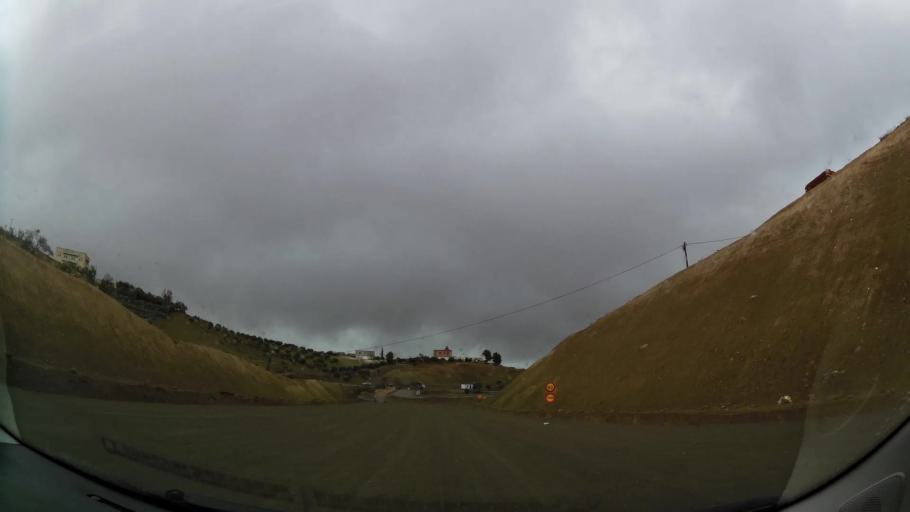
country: MA
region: Oriental
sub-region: Nador
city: Midar
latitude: 34.8914
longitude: -3.7610
